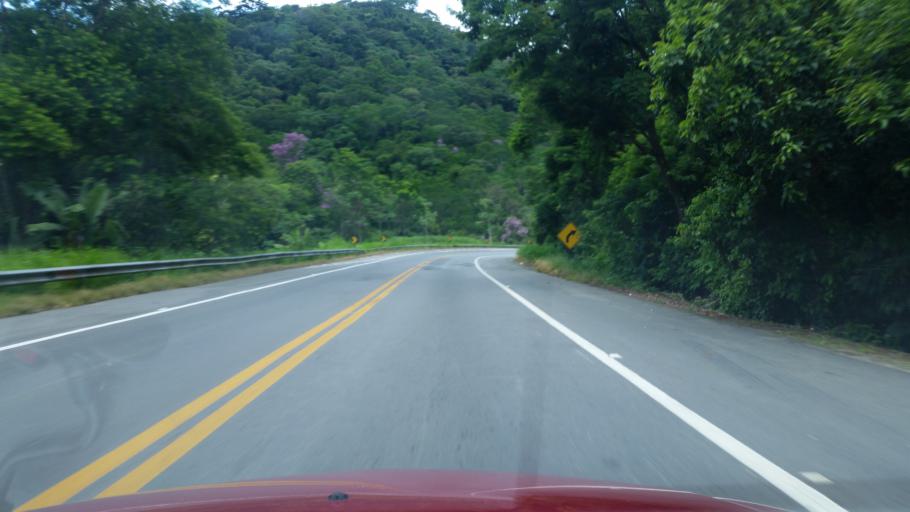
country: BR
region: Sao Paulo
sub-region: Miracatu
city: Miracatu
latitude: -24.2650
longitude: -47.3045
